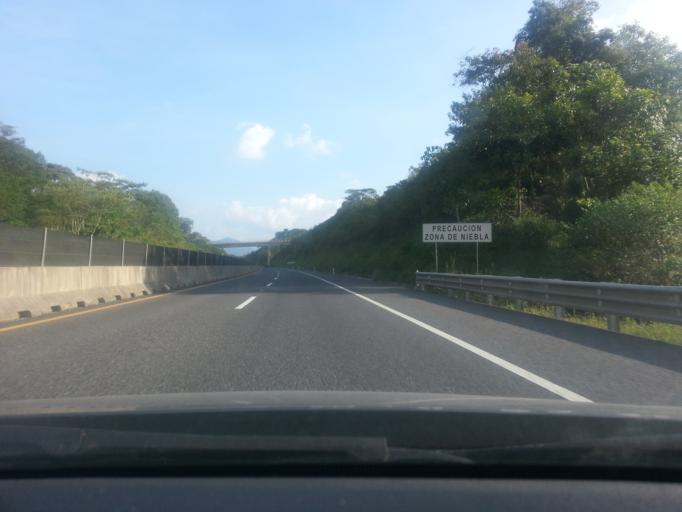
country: MX
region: Puebla
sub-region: Xicotepec
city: San Lorenzo
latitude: 20.3980
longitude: -97.9449
